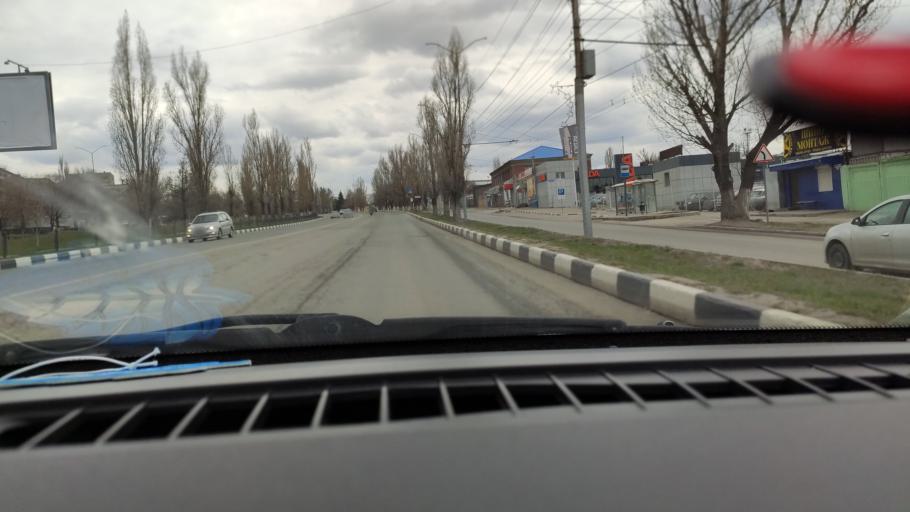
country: RU
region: Saratov
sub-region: Saratovskiy Rayon
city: Saratov
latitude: 51.6087
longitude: 45.9693
